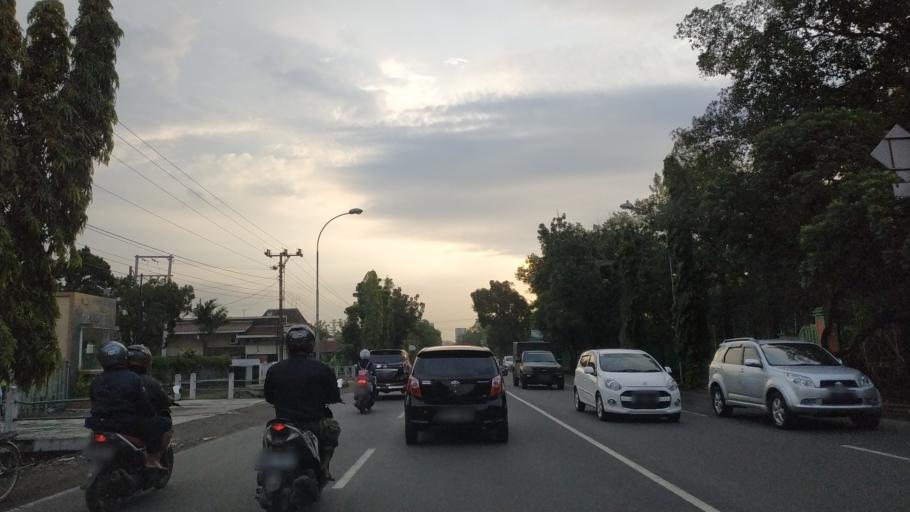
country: ID
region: Central Java
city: Kudus
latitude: -6.8039
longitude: 110.8612
